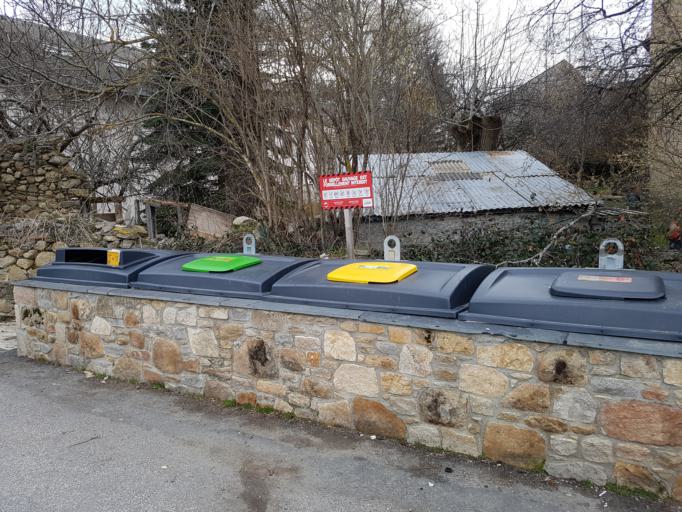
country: ES
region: Catalonia
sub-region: Provincia de Girona
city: Llivia
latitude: 42.6140
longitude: 2.1037
